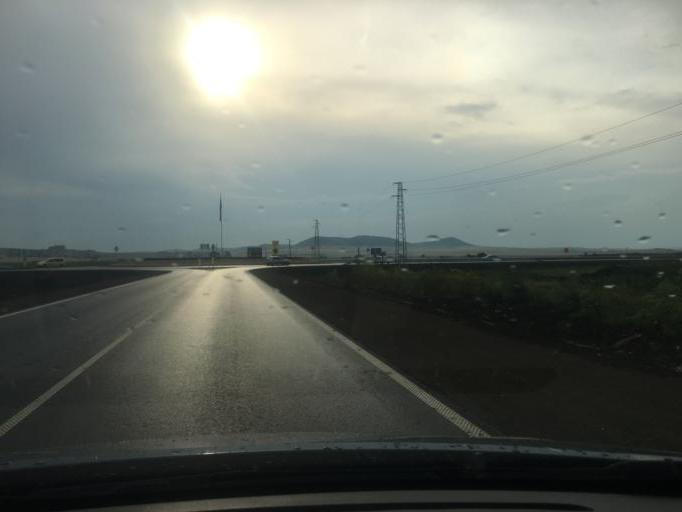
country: BG
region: Burgas
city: Aheloy
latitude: 42.6454
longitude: 27.6382
